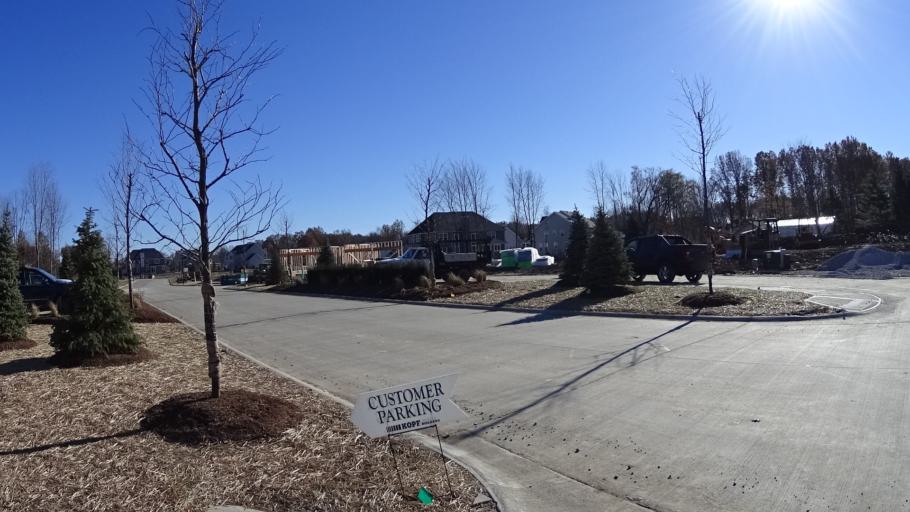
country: US
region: Ohio
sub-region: Lorain County
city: Avon Lake
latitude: 41.4857
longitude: -82.0185
